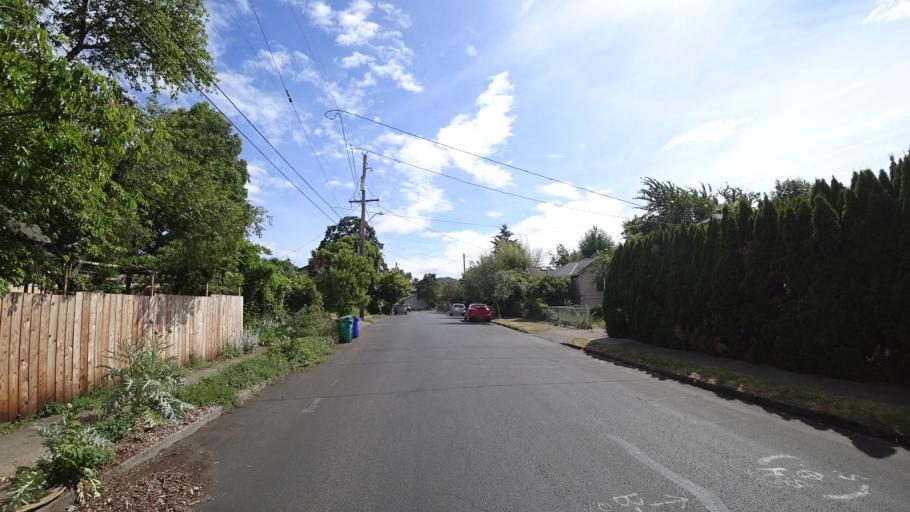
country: US
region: Oregon
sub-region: Washington County
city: West Haven
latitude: 45.5940
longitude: -122.7504
